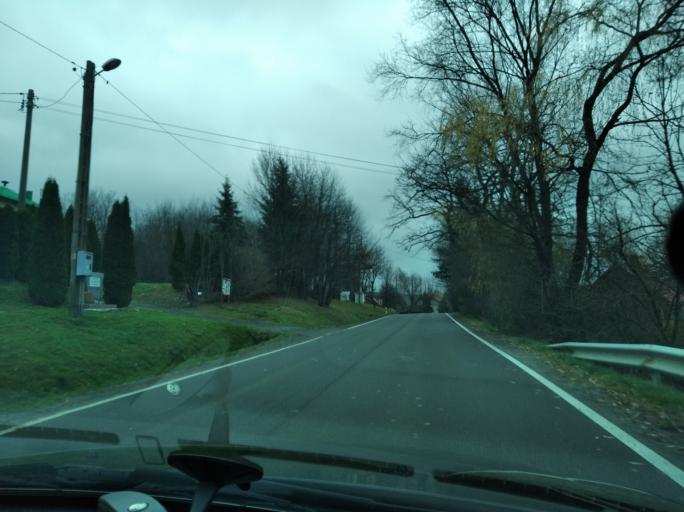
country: PL
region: Subcarpathian Voivodeship
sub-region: Powiat przeworski
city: Jawornik Polski
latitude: 49.9149
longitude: 22.2998
